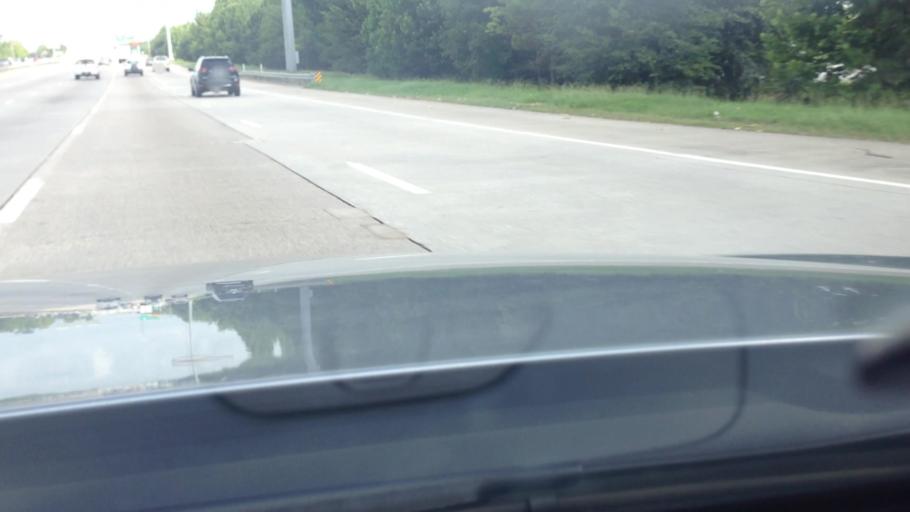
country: US
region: Texas
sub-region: Harris County
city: Hudson
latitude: 29.9472
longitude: -95.5292
